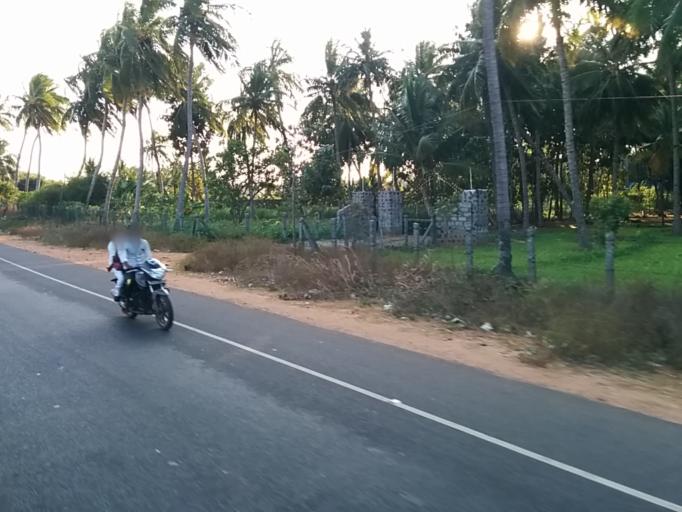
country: IN
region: Tamil Nadu
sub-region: Villupuram
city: Auroville
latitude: 12.0028
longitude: 79.8537
